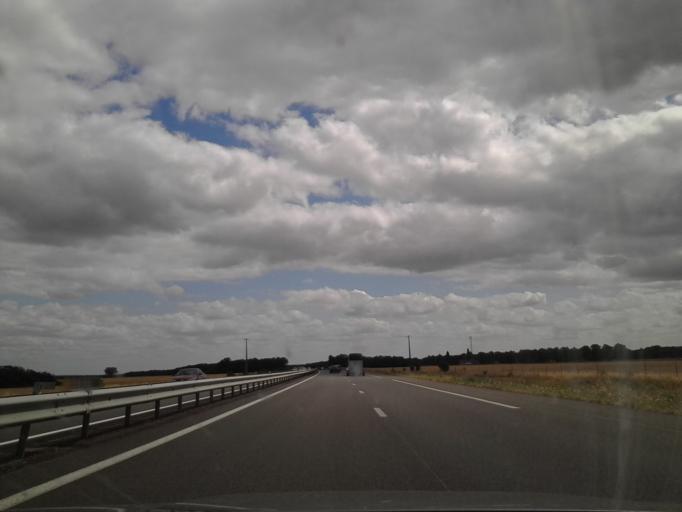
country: FR
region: Centre
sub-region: Departement du Cher
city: Levet
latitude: 46.9028
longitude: 2.4167
